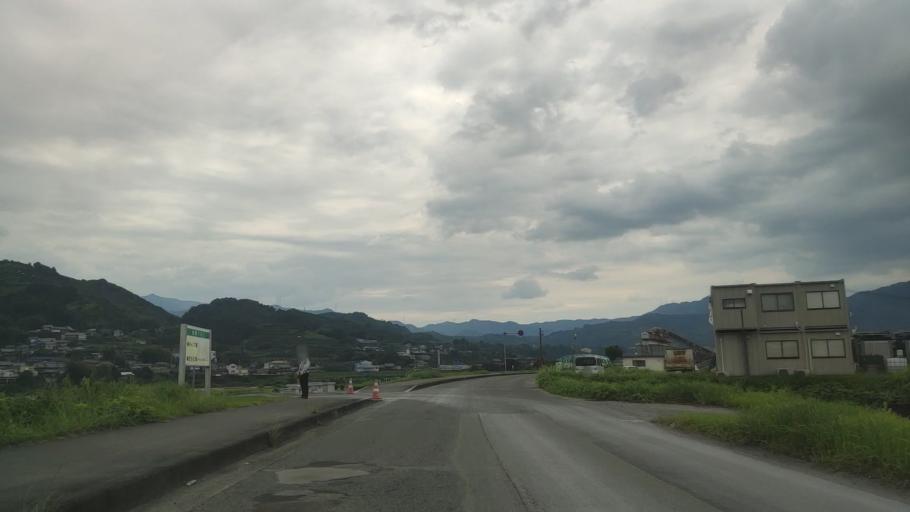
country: JP
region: Wakayama
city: Hashimoto
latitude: 34.3027
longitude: 135.5813
